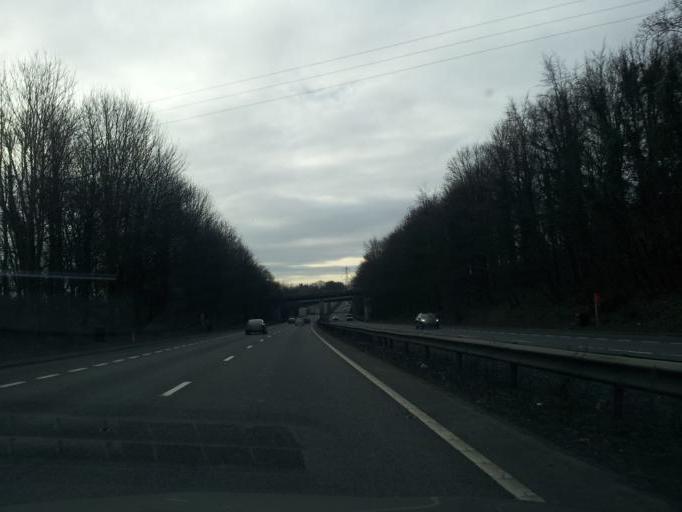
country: GB
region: England
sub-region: Lincolnshire
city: Grantham
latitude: 52.8802
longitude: -0.6354
